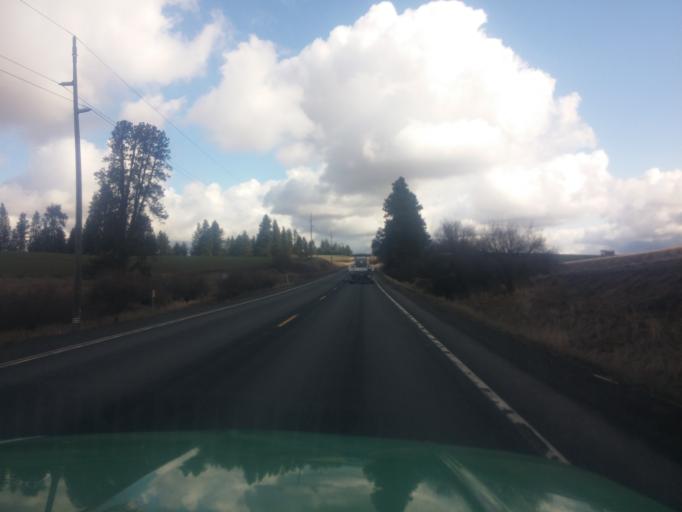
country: US
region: Idaho
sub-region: Latah County
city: Moscow
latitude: 46.9044
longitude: -116.9721
